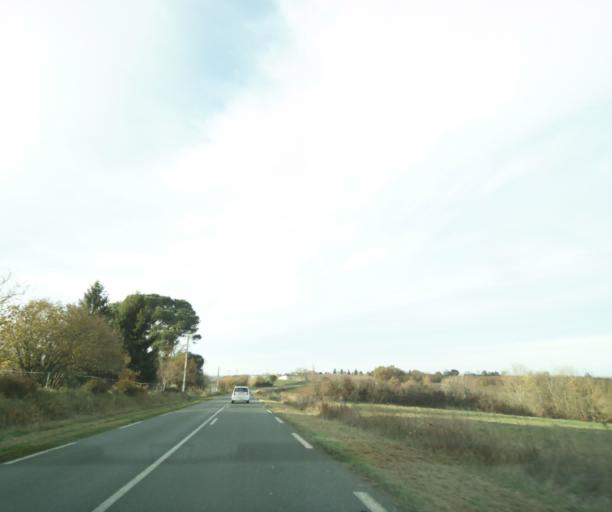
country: FR
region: Midi-Pyrenees
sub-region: Departement du Gers
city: Eauze
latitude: 43.8044
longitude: 0.0980
